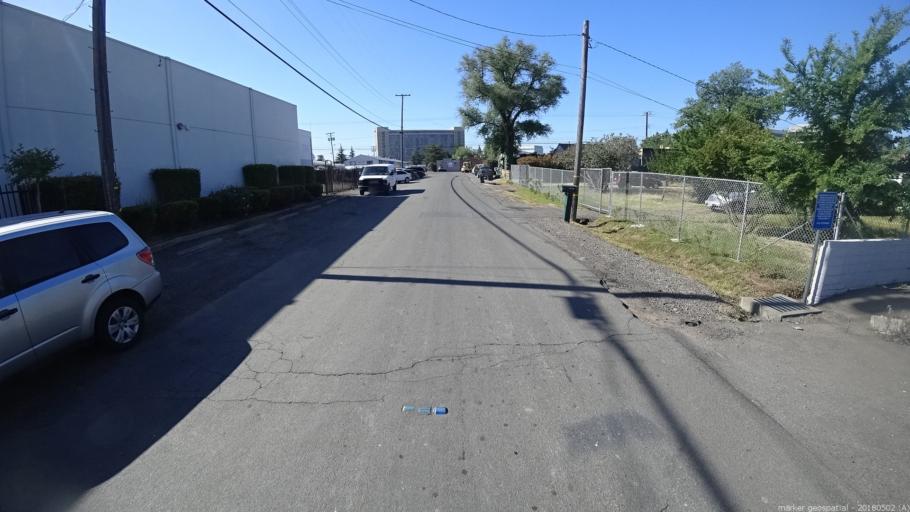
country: US
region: California
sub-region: Sacramento County
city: Arden-Arcade
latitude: 38.6094
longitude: -121.4339
